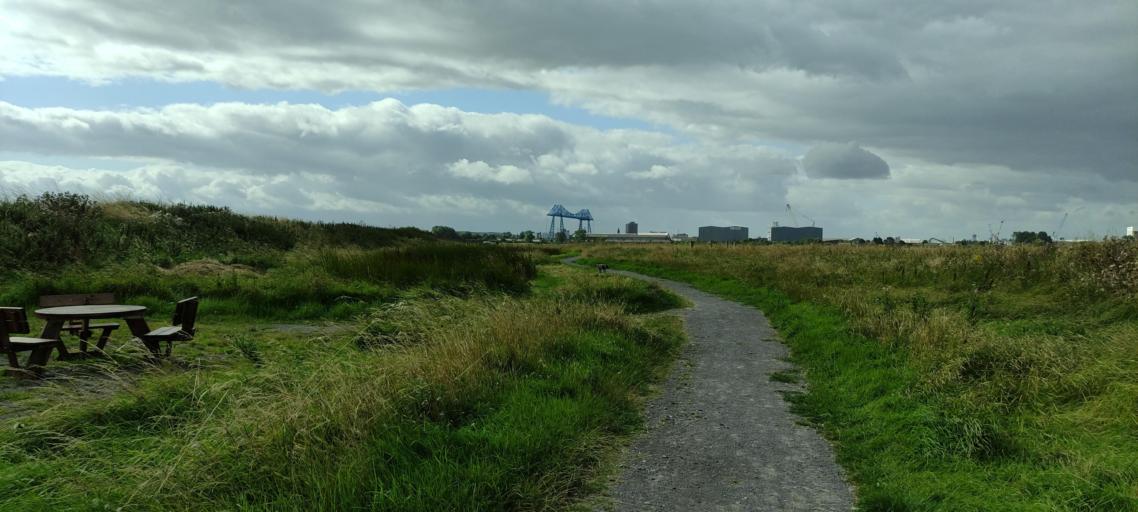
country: GB
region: England
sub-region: Middlesbrough
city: Middlesbrough
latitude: 54.5976
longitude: -1.2216
